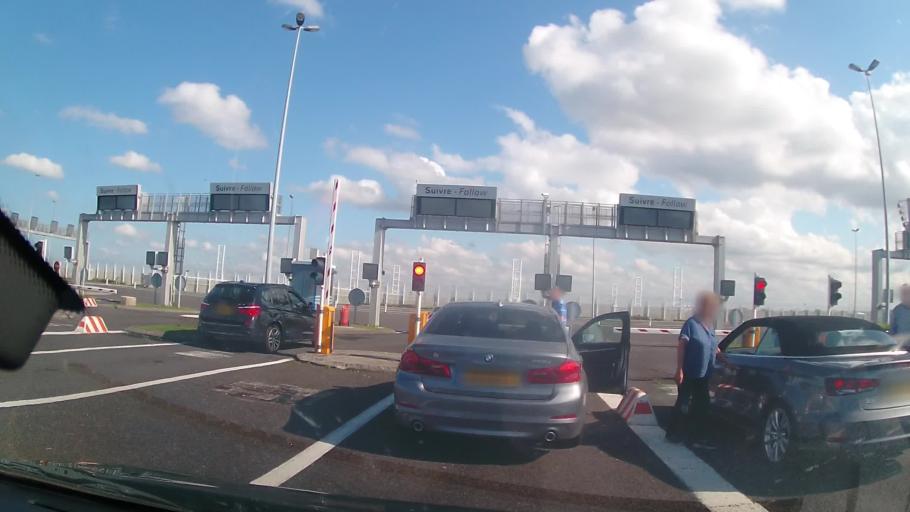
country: FR
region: Nord-Pas-de-Calais
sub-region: Departement du Pas-de-Calais
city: Frethun
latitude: 50.9263
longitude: 1.8131
